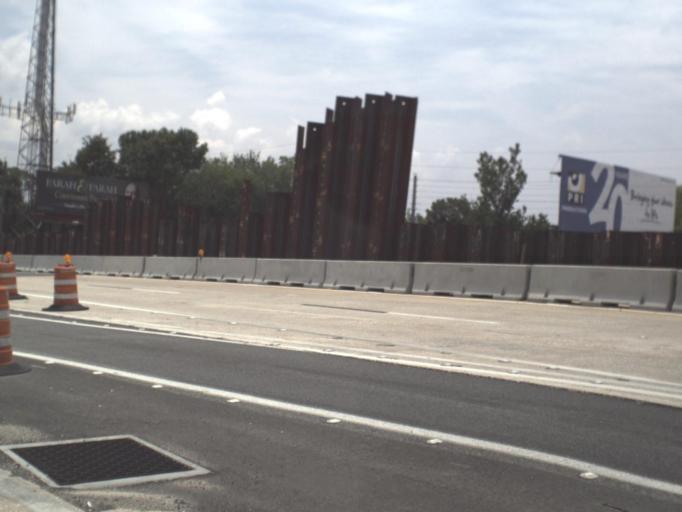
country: US
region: Florida
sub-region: Duval County
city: Jacksonville
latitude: 30.3111
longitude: -81.6496
